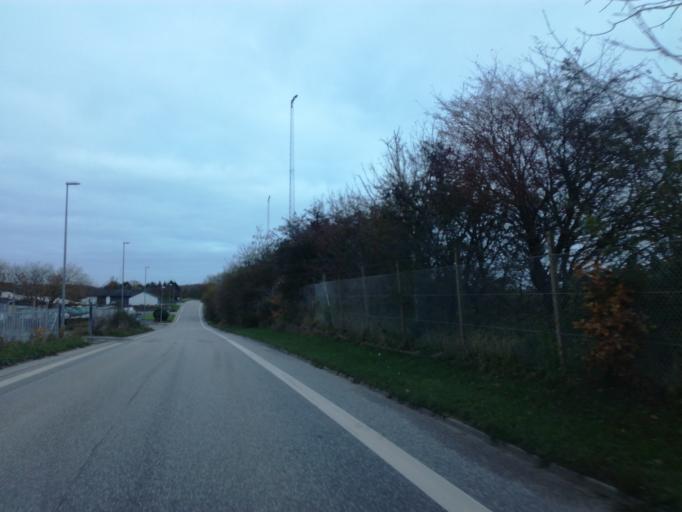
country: DK
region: South Denmark
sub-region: Fredericia Kommune
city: Snoghoj
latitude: 55.5463
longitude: 9.6867
